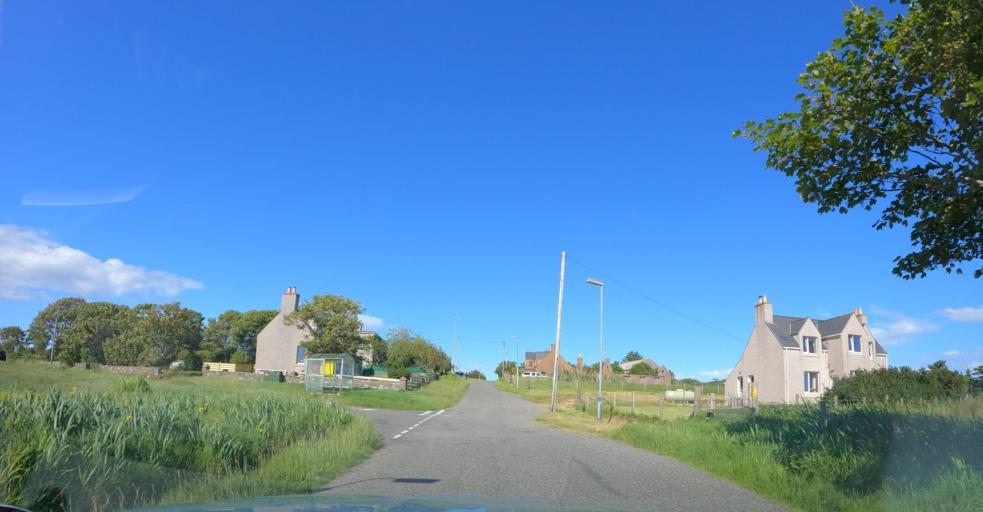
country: GB
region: Scotland
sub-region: Eilean Siar
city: Stornoway
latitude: 58.2020
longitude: -6.2206
